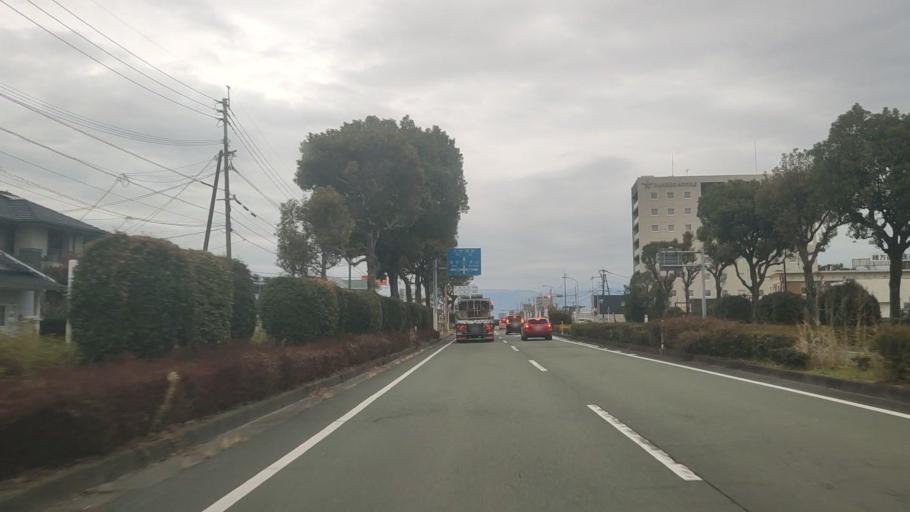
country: JP
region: Kumamoto
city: Ozu
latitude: 32.8592
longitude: 130.7979
